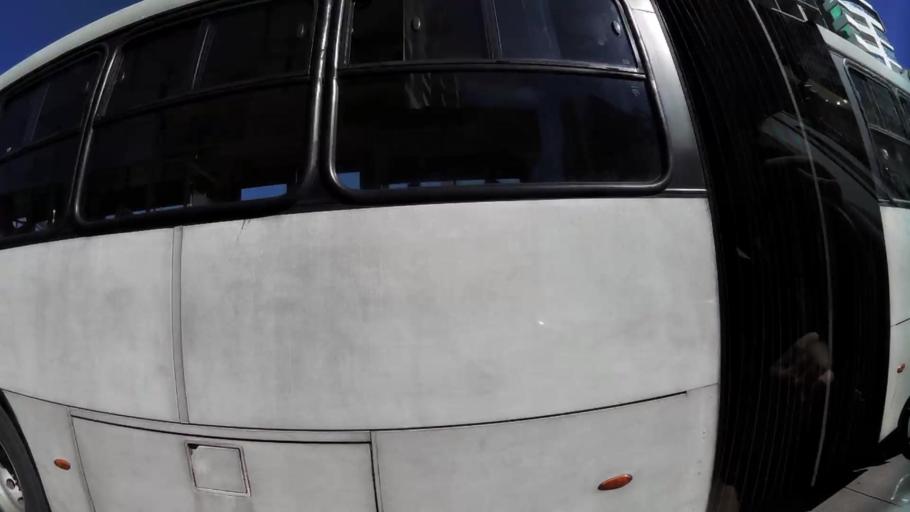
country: EC
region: Pichincha
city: Quito
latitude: -0.1888
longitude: -78.4804
